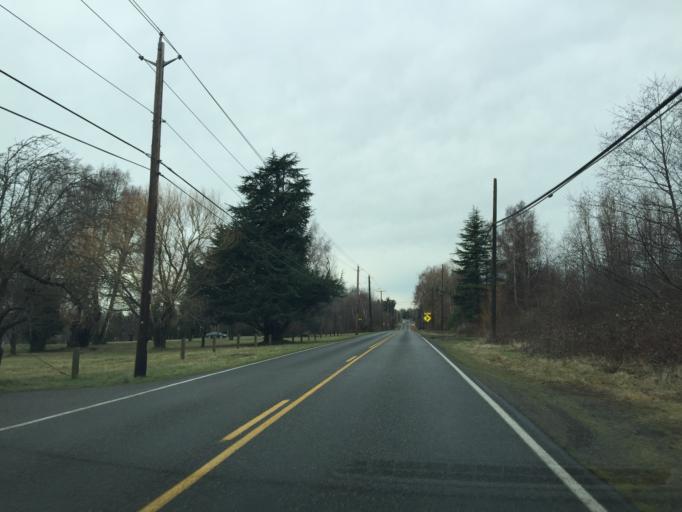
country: US
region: Washington
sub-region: Whatcom County
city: Marietta-Alderwood
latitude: 48.7778
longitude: -122.5367
